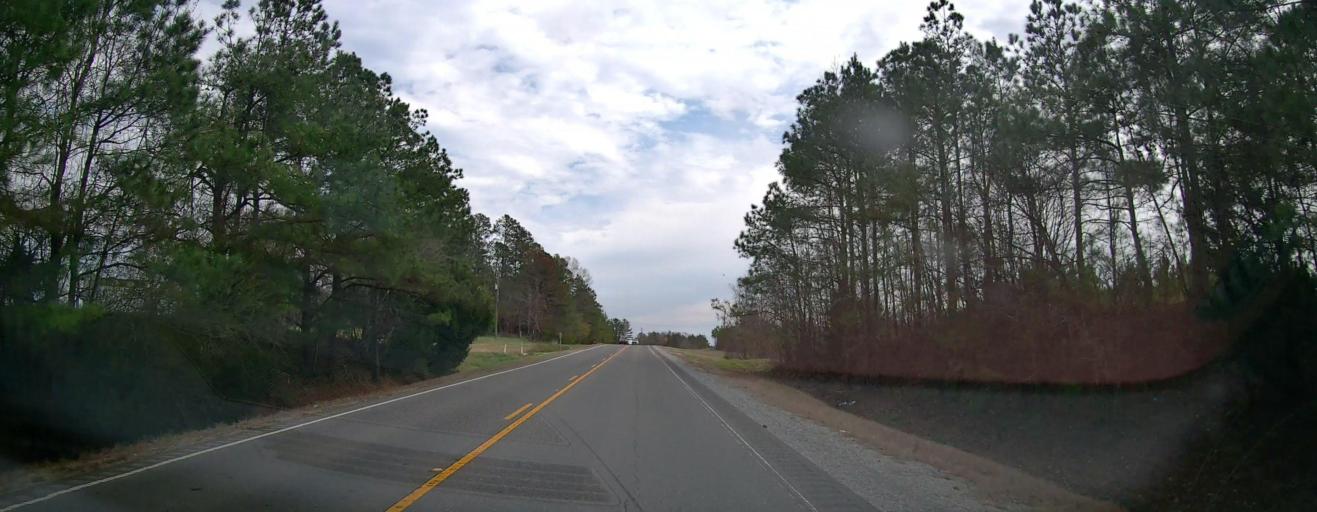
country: US
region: Alabama
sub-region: Marion County
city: Guin
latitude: 34.0409
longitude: -87.9537
